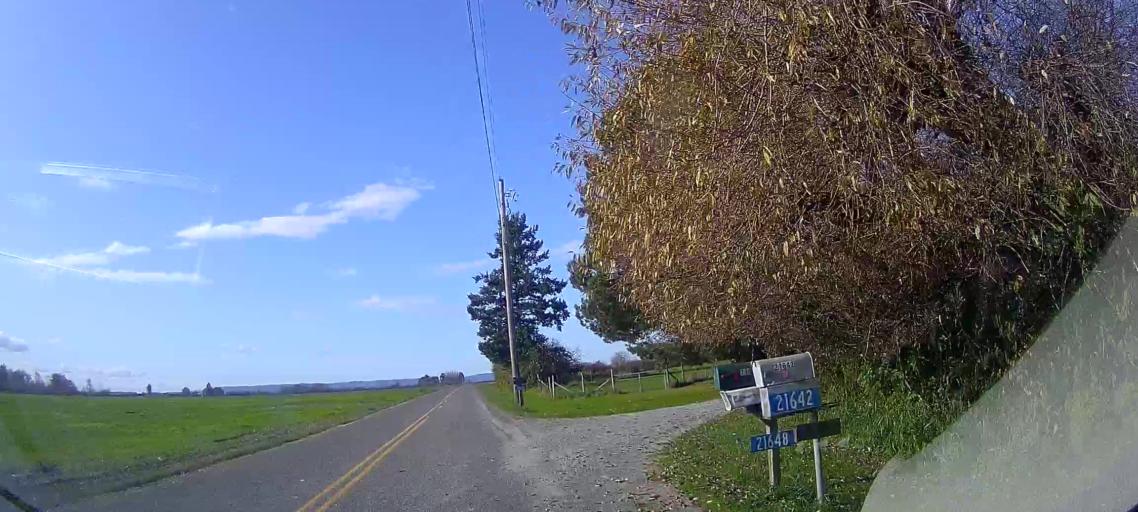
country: US
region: Washington
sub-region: Snohomish County
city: Stanwood
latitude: 48.3299
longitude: -122.3704
